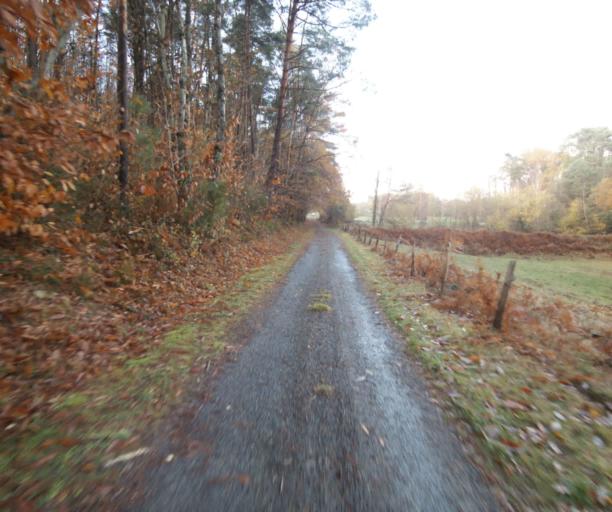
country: FR
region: Limousin
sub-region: Departement de la Correze
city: Cornil
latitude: 45.2162
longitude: 1.6785
